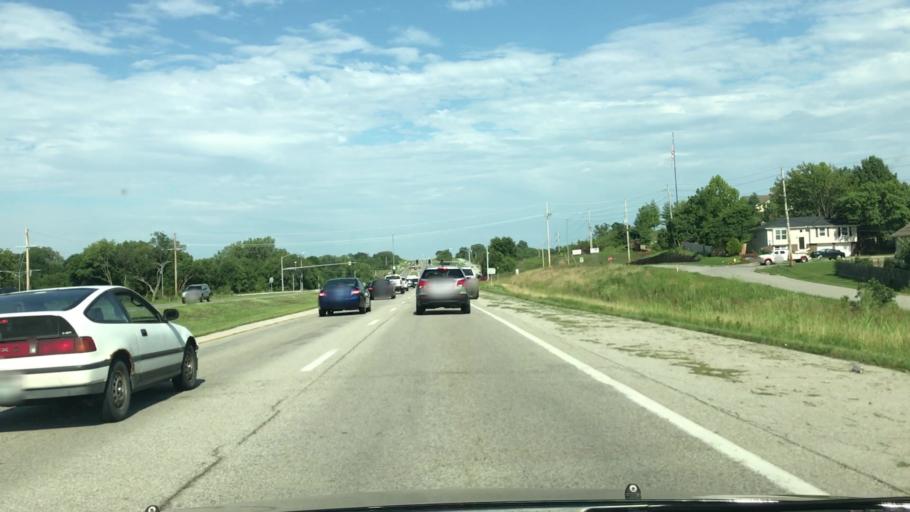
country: US
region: Missouri
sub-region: Jackson County
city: Grandview
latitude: 38.8578
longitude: -94.5195
